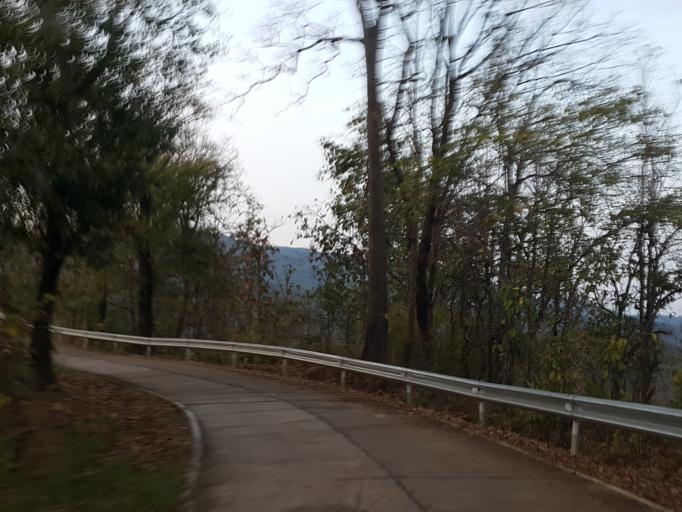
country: TH
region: Lampang
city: Mueang Pan
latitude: 18.8162
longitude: 99.4727
